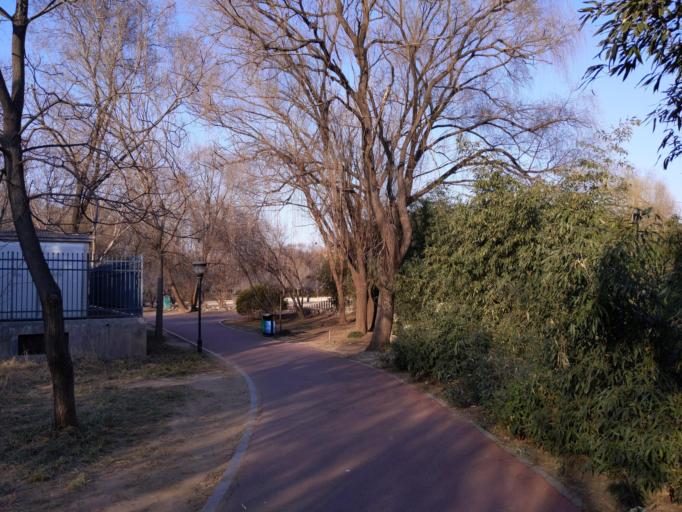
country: CN
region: Henan Sheng
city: Puyang
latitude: 35.7768
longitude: 114.9598
